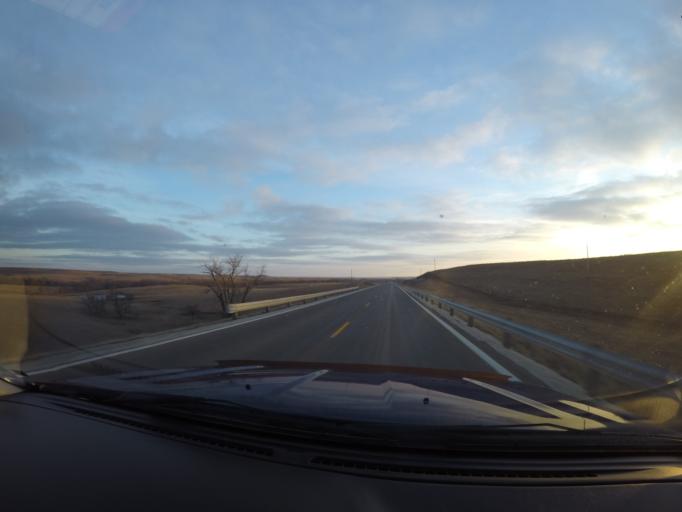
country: US
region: Kansas
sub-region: Chase County
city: Cottonwood Falls
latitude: 38.4929
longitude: -96.5573
